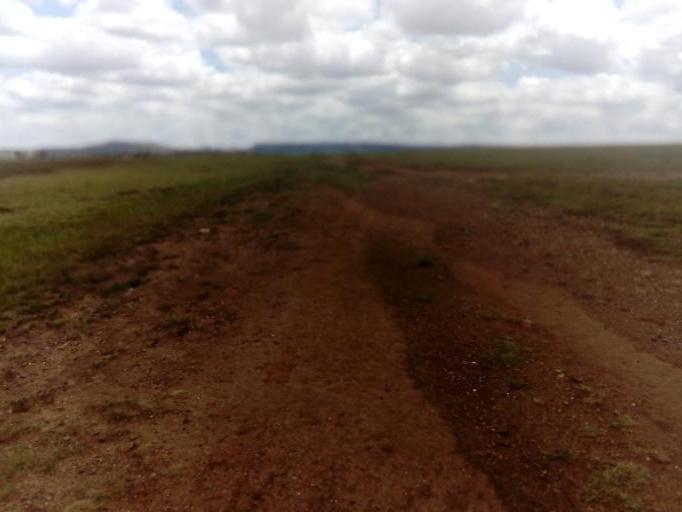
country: LS
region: Berea
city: Teyateyaneng
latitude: -29.1235
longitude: 27.7606
